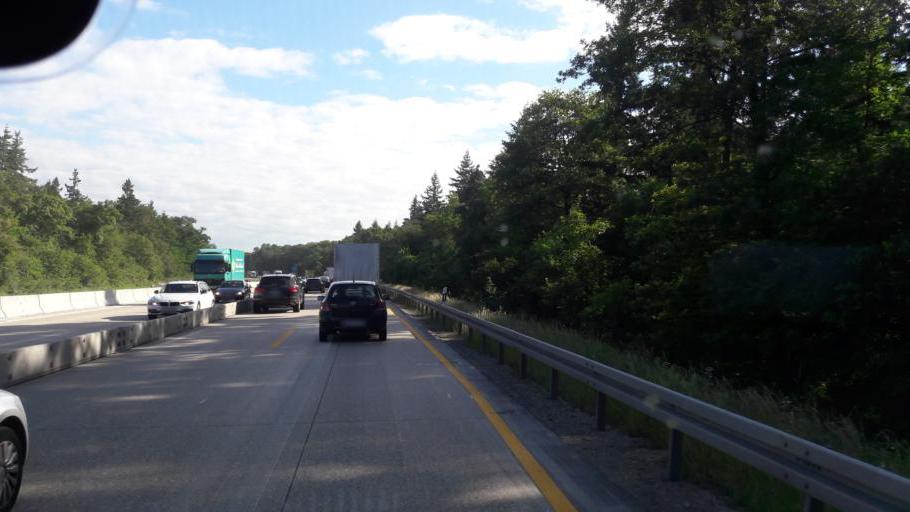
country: DE
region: Baden-Wuerttemberg
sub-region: Karlsruhe Region
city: Karlsdorf-Neuthard
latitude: 49.1130
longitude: 8.5495
